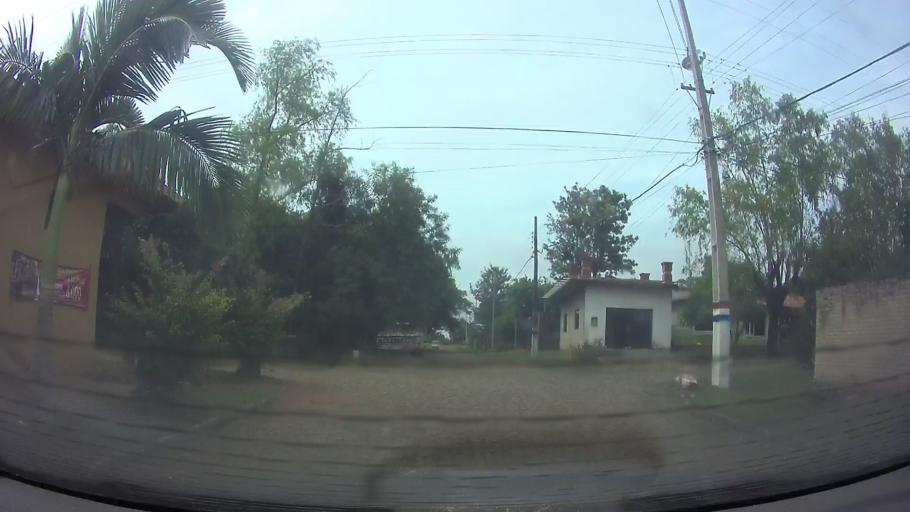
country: PY
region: Cordillera
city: Atyra
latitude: -25.2794
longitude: -57.1767
